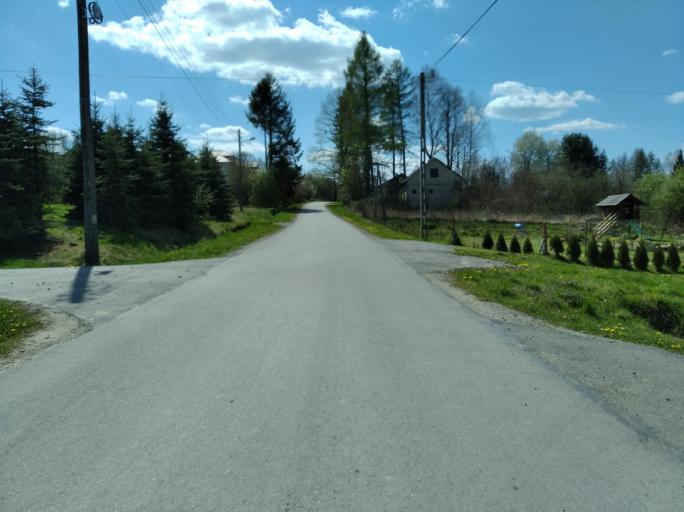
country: PL
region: Subcarpathian Voivodeship
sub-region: Powiat brzozowski
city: Domaradz
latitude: 49.7889
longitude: 21.9623
